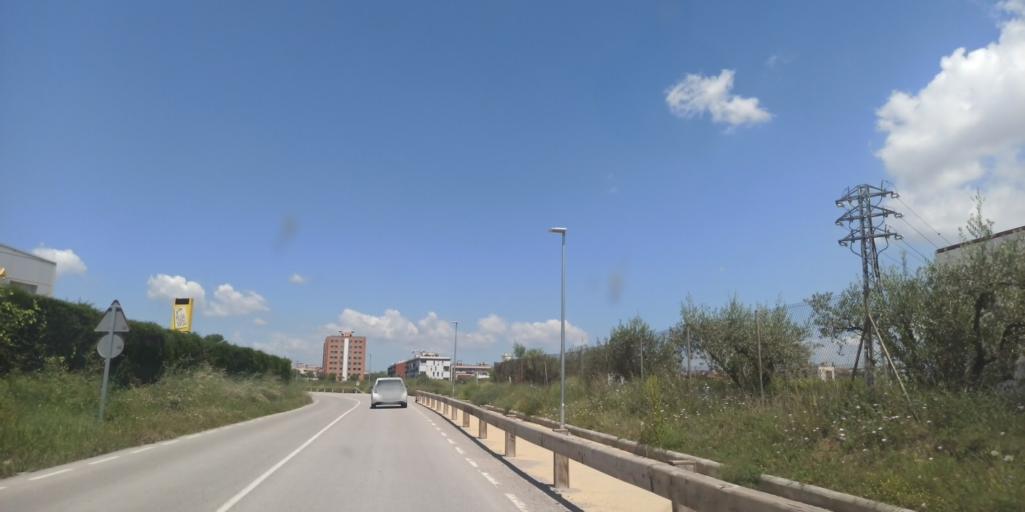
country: ES
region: Catalonia
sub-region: Provincia de Barcelona
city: Vilafranca del Penedes
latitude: 41.3317
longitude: 1.6979
